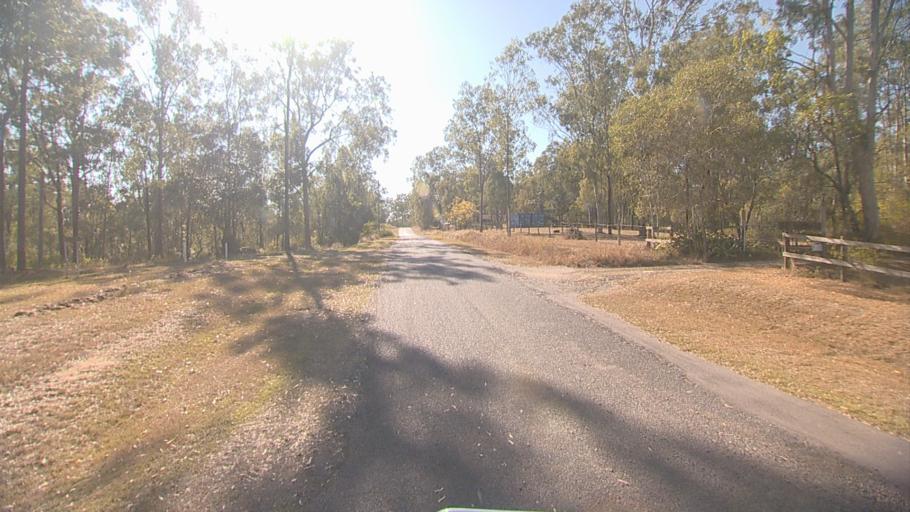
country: AU
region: Queensland
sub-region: Logan
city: Cedar Vale
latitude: -27.8474
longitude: 153.0572
